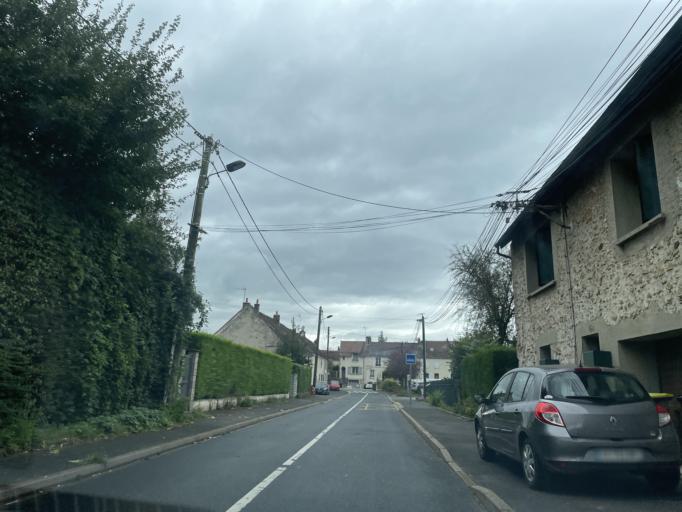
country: FR
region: Ile-de-France
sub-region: Departement de Seine-et-Marne
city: Chailly-en-Brie
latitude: 48.8120
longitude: 3.1116
